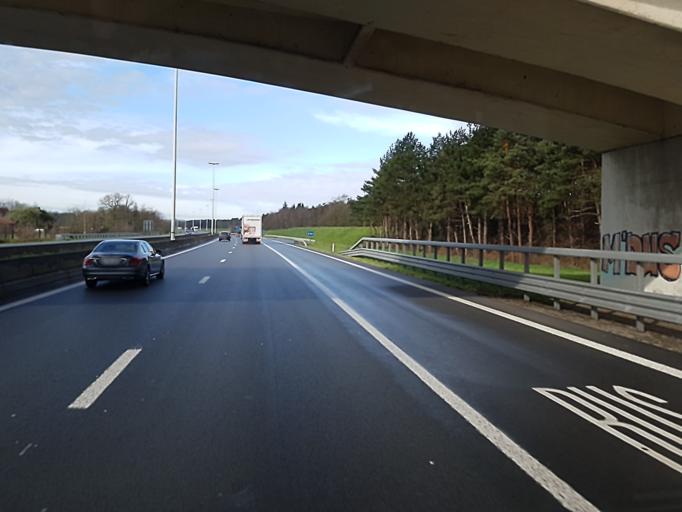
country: BE
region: Flanders
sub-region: Provincie Antwerpen
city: Zandhoven
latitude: 51.2406
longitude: 4.6785
